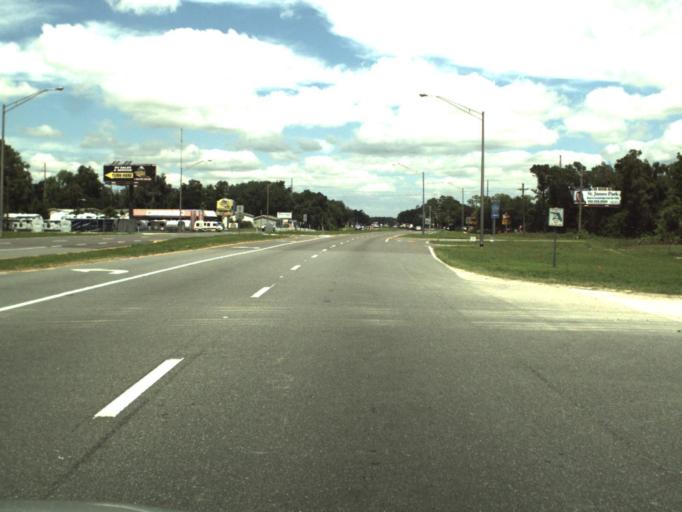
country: US
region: Florida
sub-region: Marion County
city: Ocala
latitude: 29.2171
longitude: -82.1456
